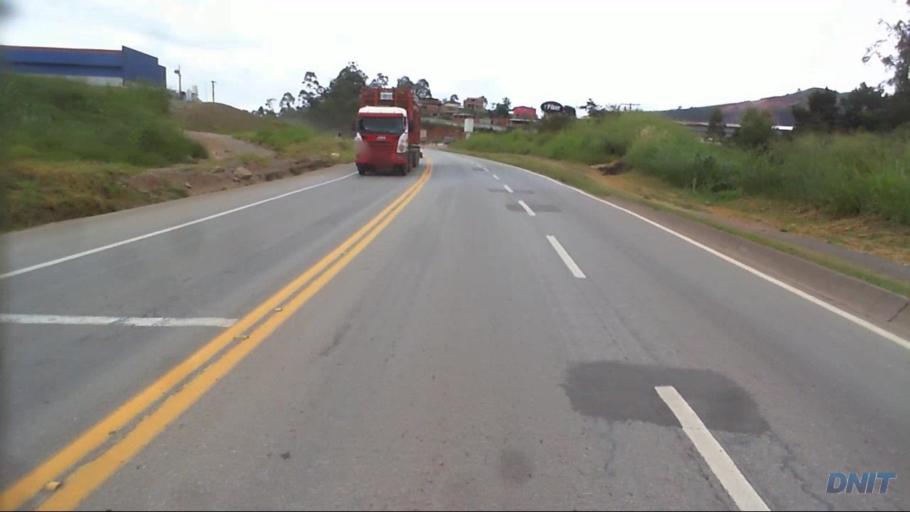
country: BR
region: Minas Gerais
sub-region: Joao Monlevade
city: Joao Monlevade
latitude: -19.8434
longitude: -43.1695
